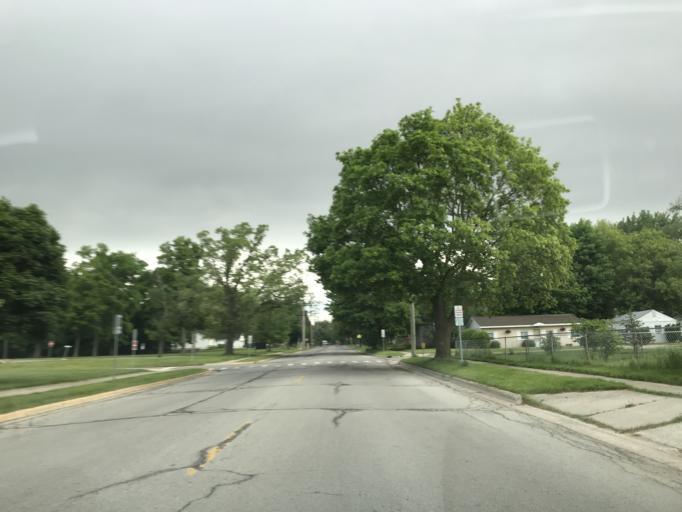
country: US
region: Michigan
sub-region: Livingston County
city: Brighton
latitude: 42.5262
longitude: -83.7923
